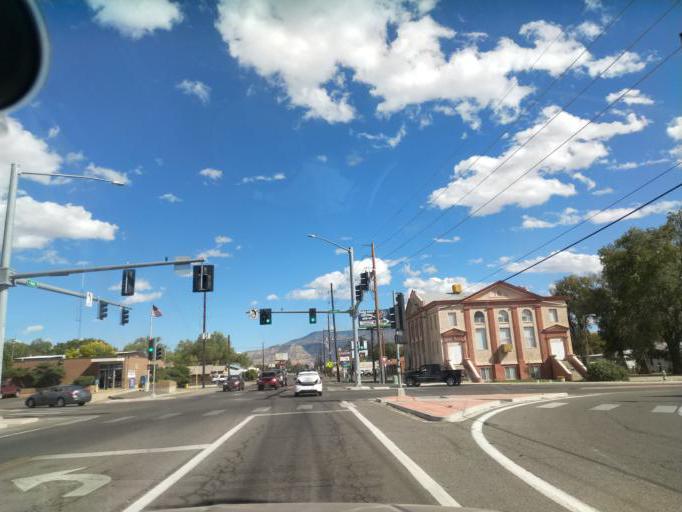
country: US
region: Colorado
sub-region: Mesa County
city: Clifton
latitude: 39.0917
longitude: -108.4507
